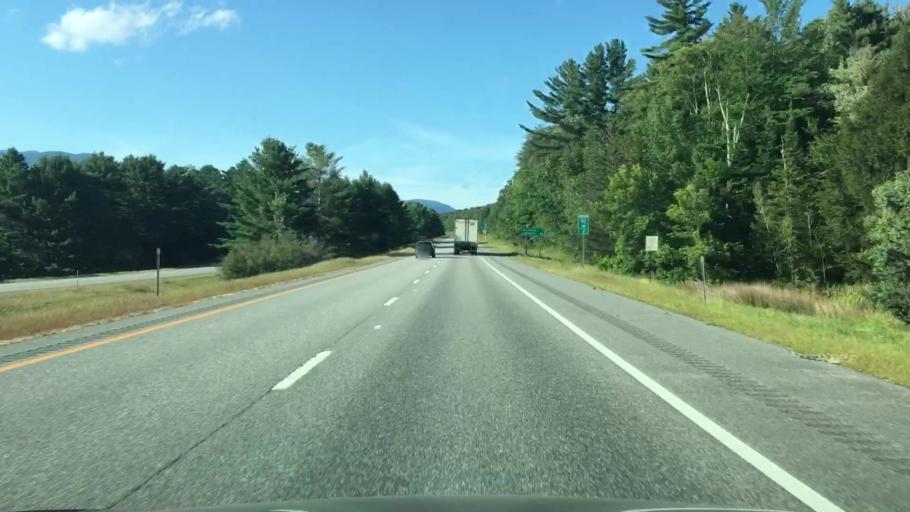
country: US
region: New Hampshire
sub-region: Grafton County
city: Woodstock
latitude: 44.0469
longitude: -71.6812
